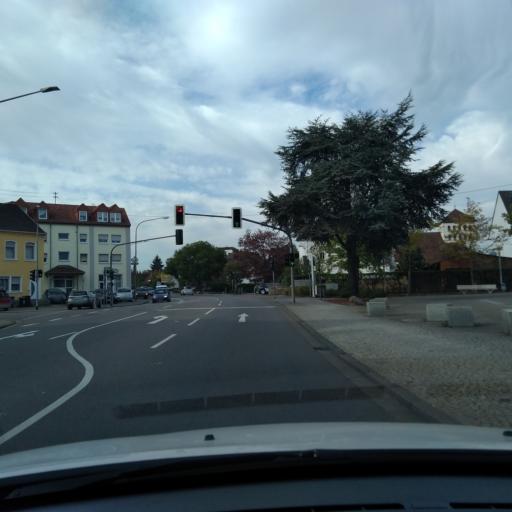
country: DE
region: Saarland
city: Saarlouis
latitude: 49.3245
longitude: 6.7680
